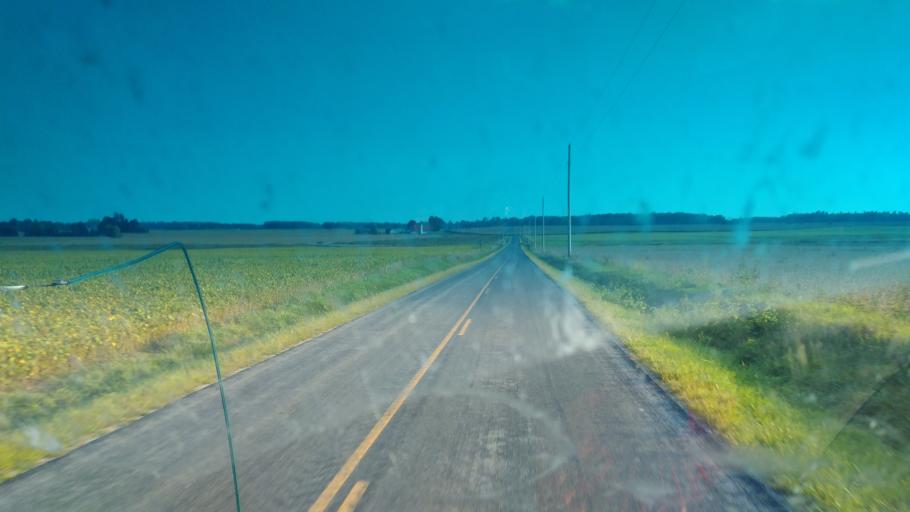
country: US
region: Ohio
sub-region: Crawford County
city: Bucyrus
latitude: 40.8919
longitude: -82.8777
